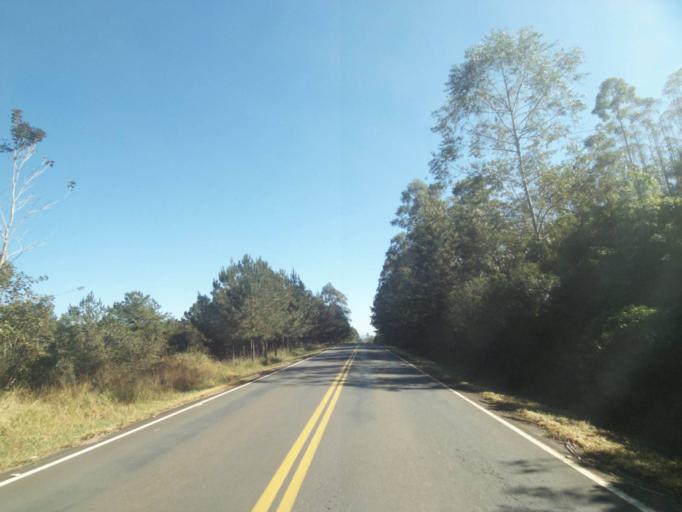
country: BR
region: Parana
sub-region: Telemaco Borba
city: Telemaco Borba
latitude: -24.4365
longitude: -50.5518
